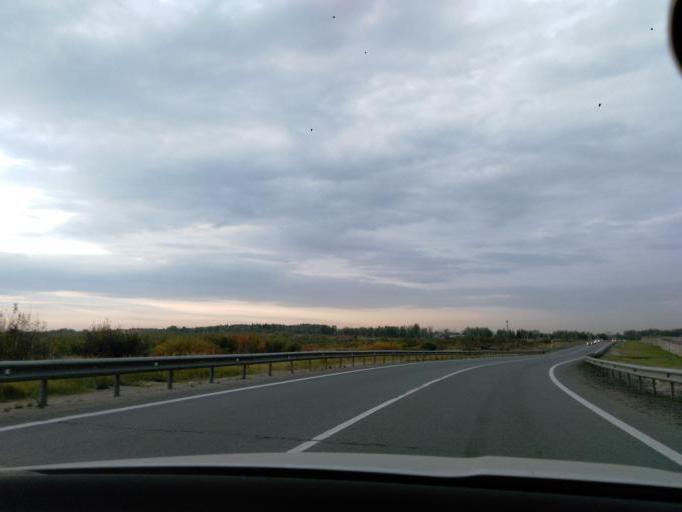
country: RU
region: Moskovskaya
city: Lobnya
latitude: 55.9812
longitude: 37.4524
